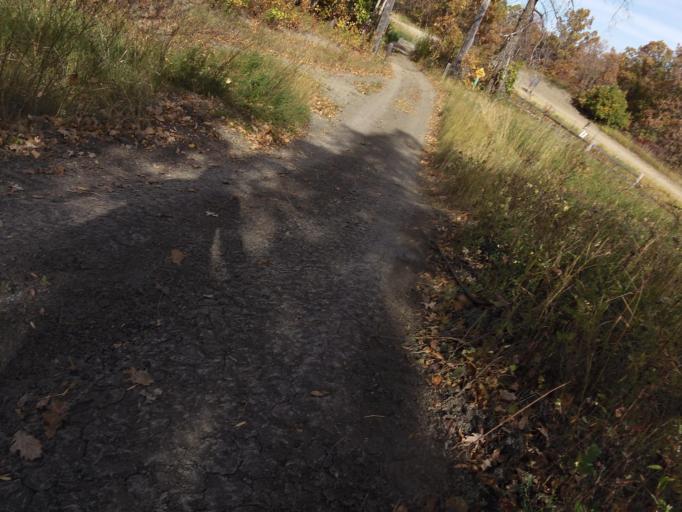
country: CA
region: Manitoba
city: Morden
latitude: 48.9489
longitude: -98.0837
